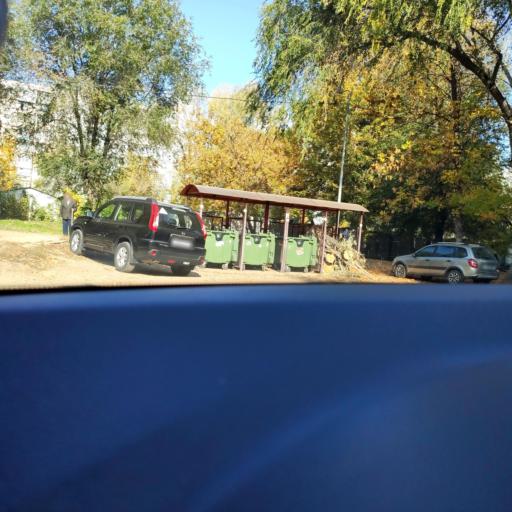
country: RU
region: Samara
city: Petra-Dubrava
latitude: 53.2452
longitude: 50.2617
